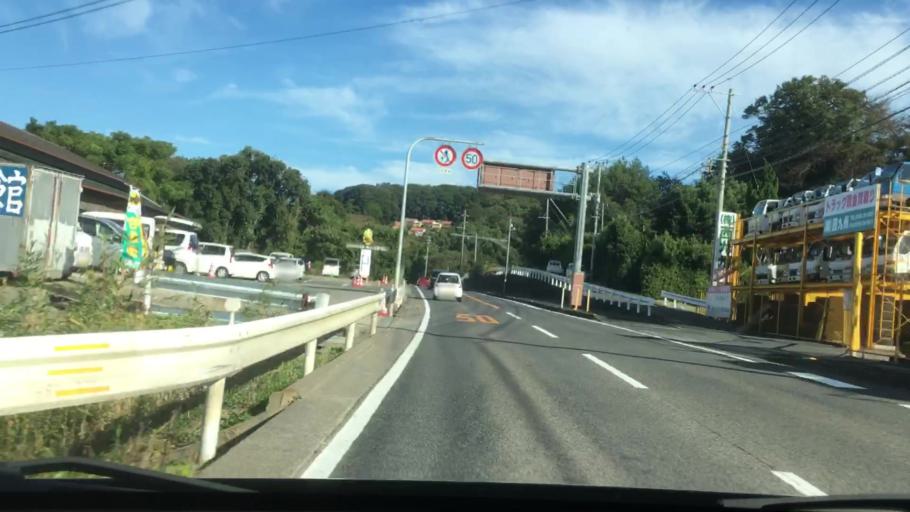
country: JP
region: Nagasaki
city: Sasebo
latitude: 33.0661
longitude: 129.7642
